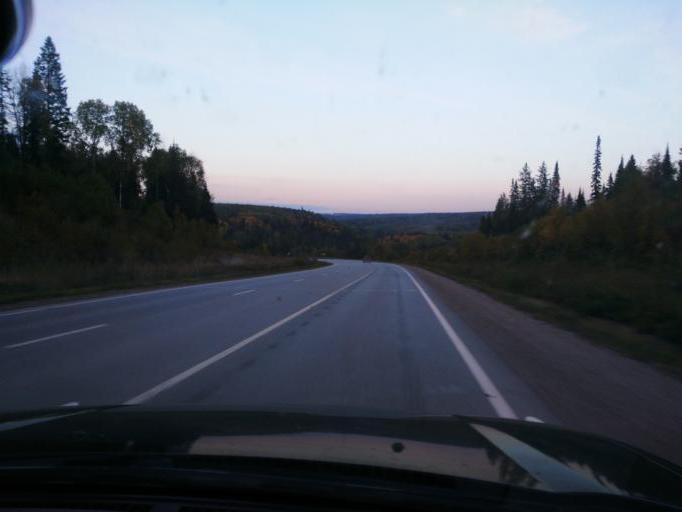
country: RU
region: Perm
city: Polazna
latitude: 58.2889
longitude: 56.5003
